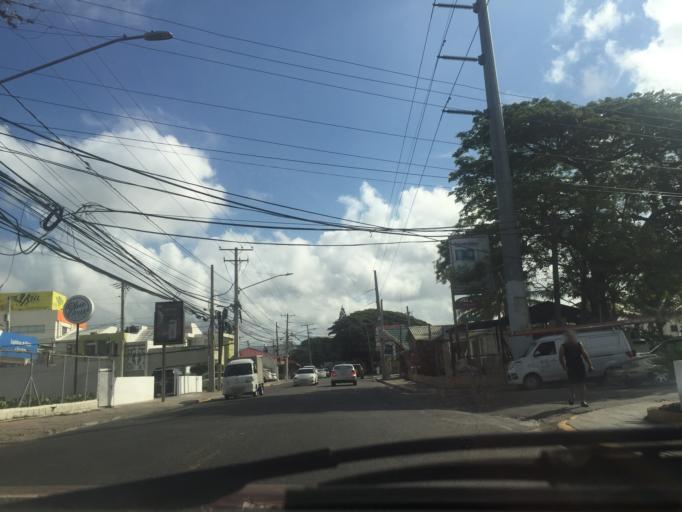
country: DO
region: Santiago
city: Santiago de los Caballeros
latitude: 19.4486
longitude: -70.6662
